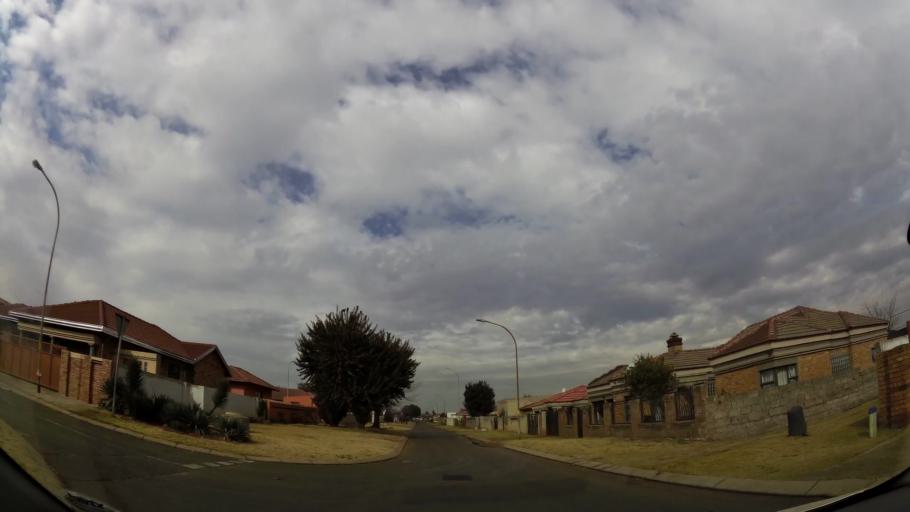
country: ZA
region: Gauteng
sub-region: Ekurhuleni Metropolitan Municipality
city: Germiston
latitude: -26.3214
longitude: 28.1758
